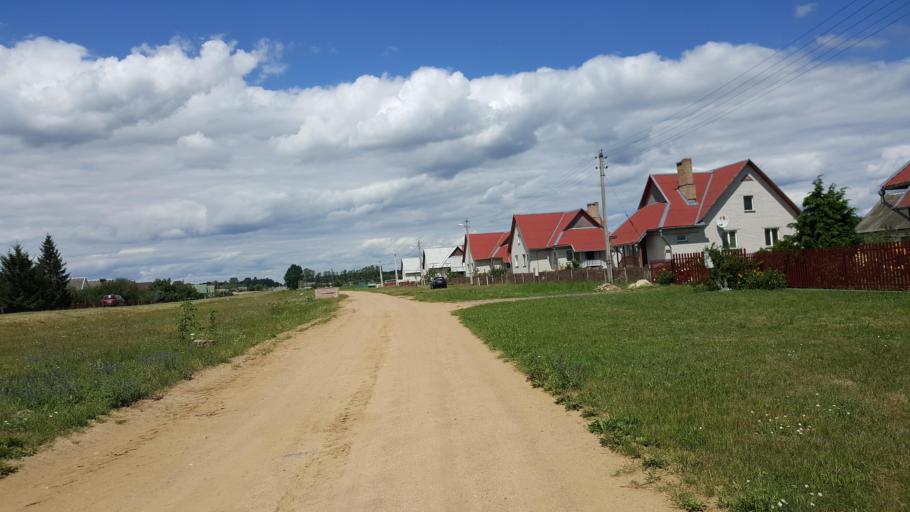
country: BY
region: Brest
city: Kamyanyets
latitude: 52.3273
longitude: 23.9172
